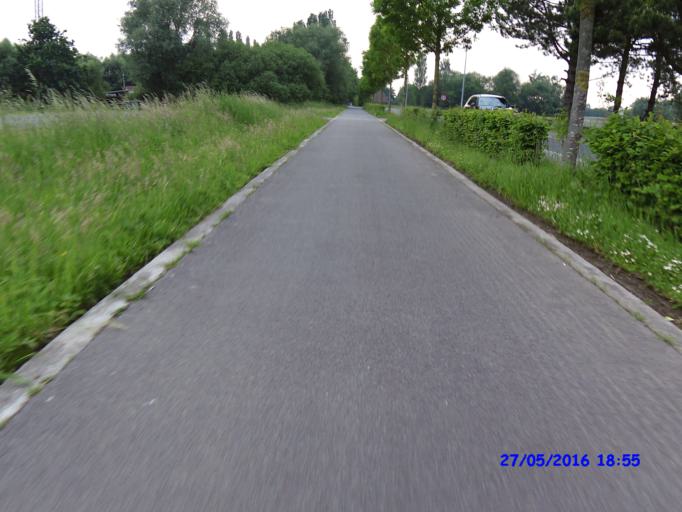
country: BE
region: Flanders
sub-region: Provincie Oost-Vlaanderen
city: Aalst
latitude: 50.9356
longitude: 4.0844
